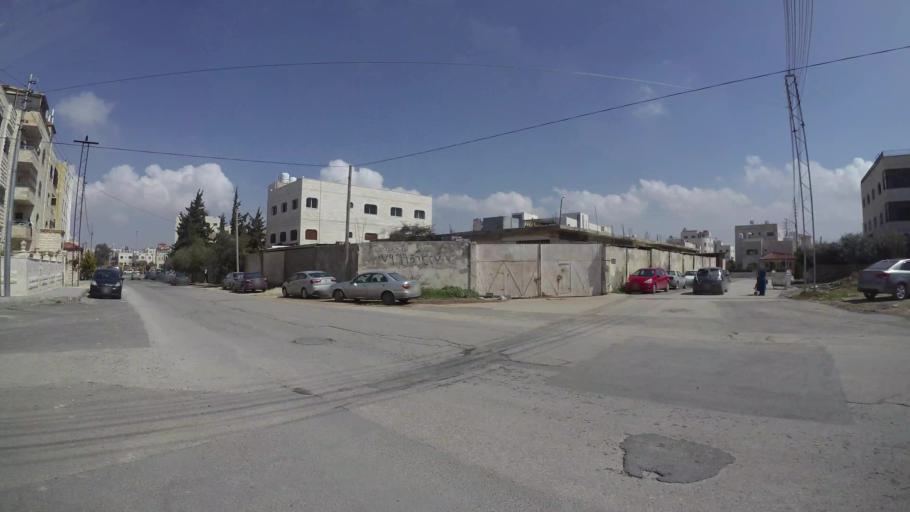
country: JO
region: Amman
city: Al Bunayyat ash Shamaliyah
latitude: 31.9018
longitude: 35.8888
